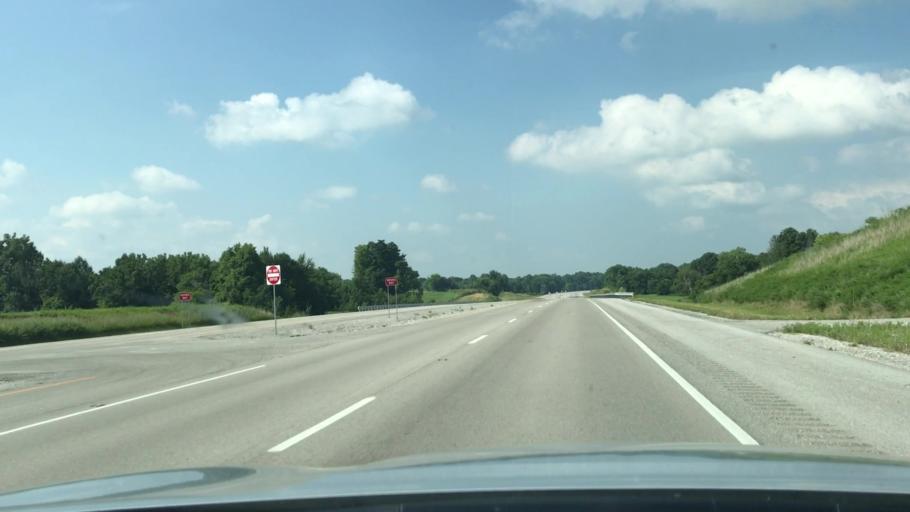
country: US
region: Kentucky
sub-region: Barren County
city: Glasgow
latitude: 37.0090
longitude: -85.9558
